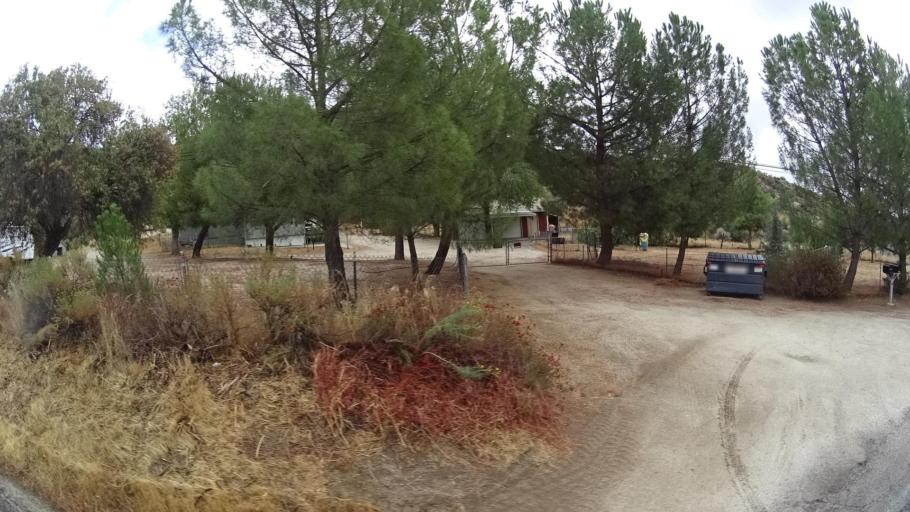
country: US
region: California
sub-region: San Diego County
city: Campo
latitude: 32.7035
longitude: -116.4324
